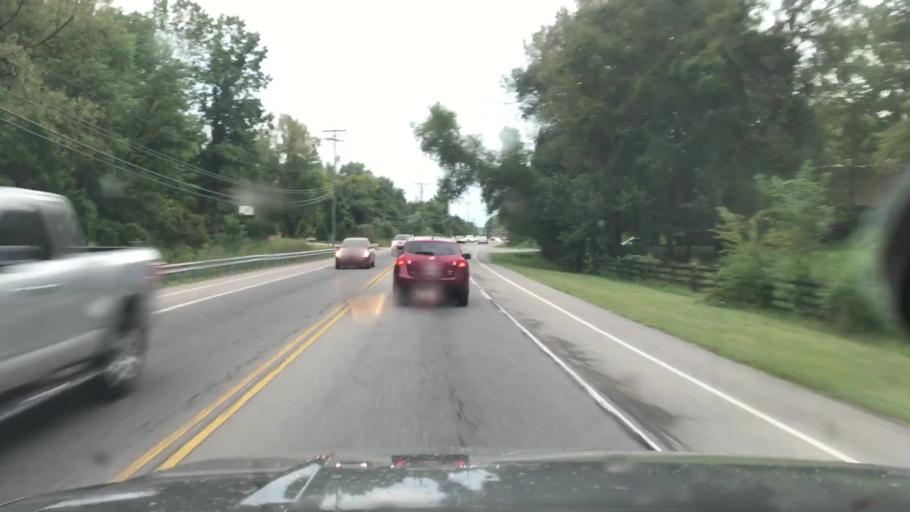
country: US
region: Tennessee
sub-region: Davidson County
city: Lakewood
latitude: 36.1284
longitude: -86.6294
